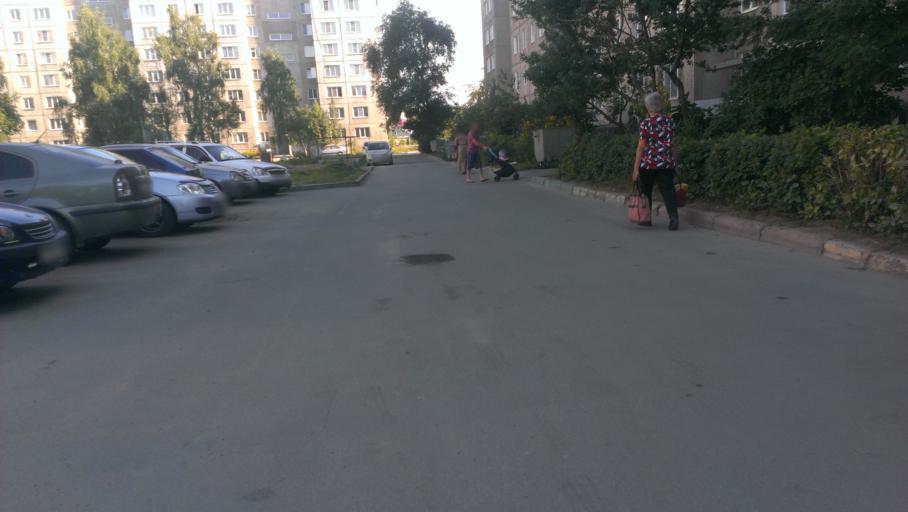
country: RU
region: Altai Krai
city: Novosilikatnyy
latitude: 53.3059
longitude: 83.6233
